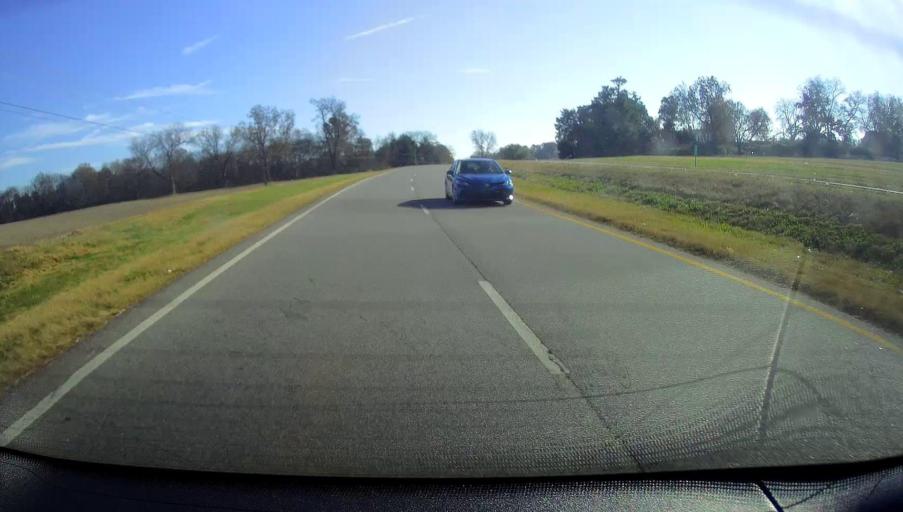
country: US
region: Alabama
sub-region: Morgan County
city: Decatur
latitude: 34.6820
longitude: -86.9499
